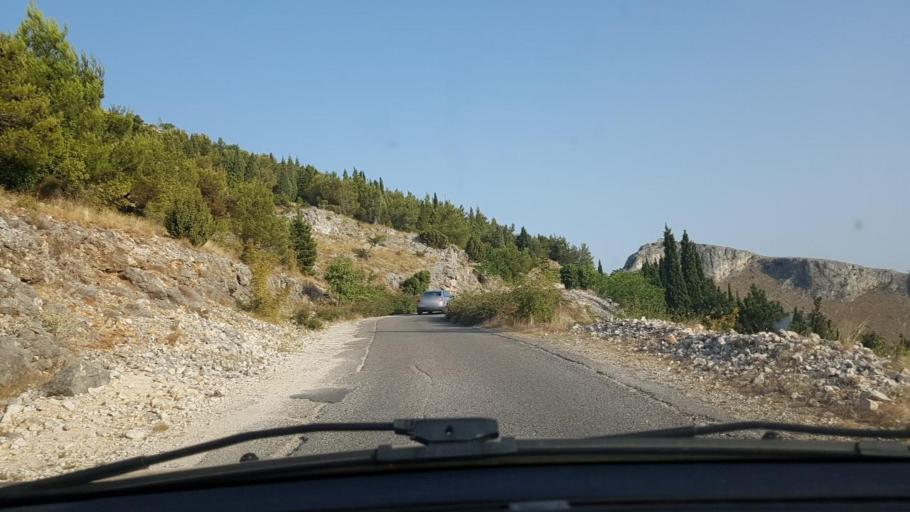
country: BA
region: Federation of Bosnia and Herzegovina
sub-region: Hercegovacko-Bosanski Kanton
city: Mostar
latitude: 43.3508
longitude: 17.8270
